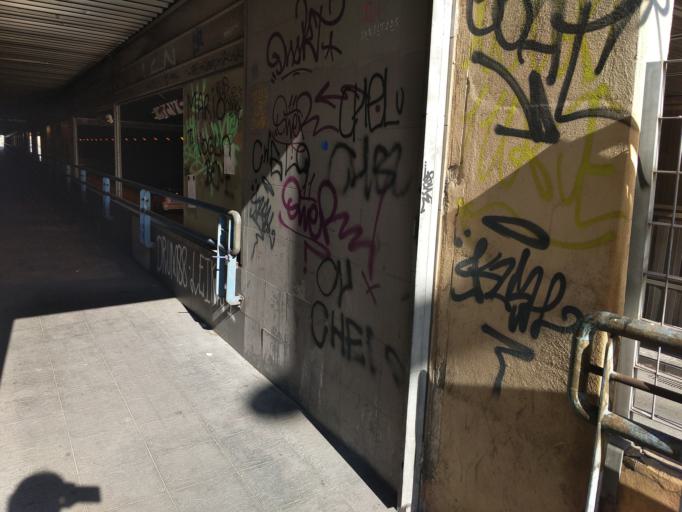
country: IT
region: Apulia
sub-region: Provincia di Bari
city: Bari
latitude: 41.1170
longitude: 16.8524
